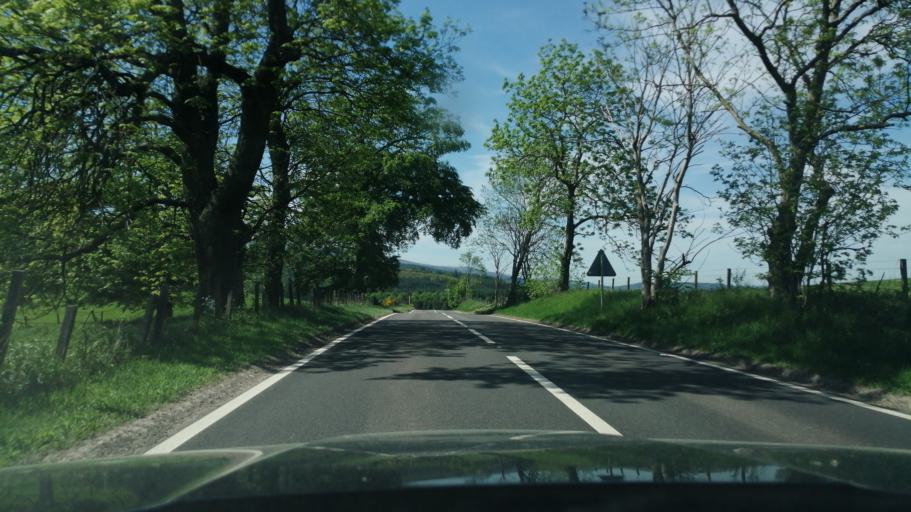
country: GB
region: Scotland
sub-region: Moray
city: Rothes
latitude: 57.4896
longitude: -3.1615
